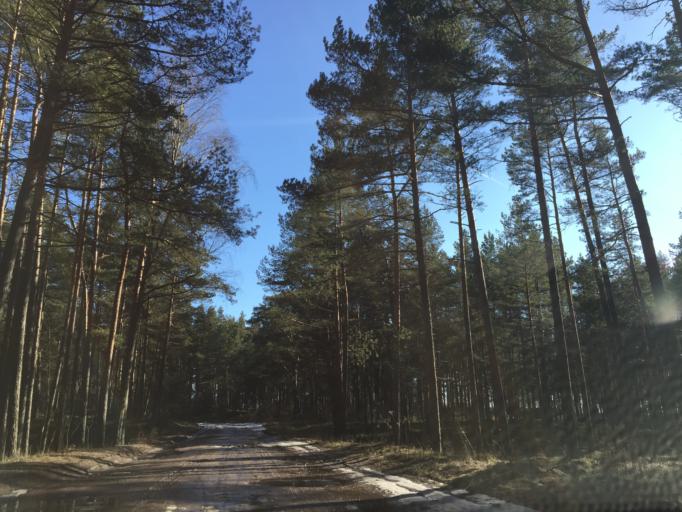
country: LV
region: Babite
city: Pinki
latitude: 56.9677
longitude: 23.8748
